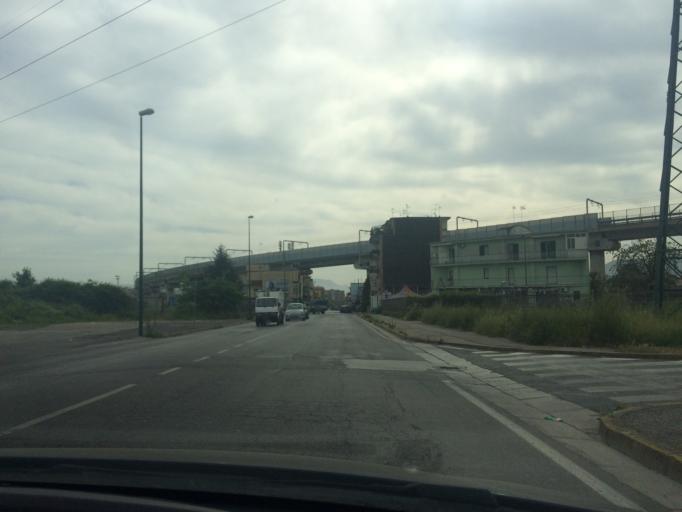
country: IT
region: Campania
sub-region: Provincia di Napoli
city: Mugnano di Napoli
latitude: 40.8939
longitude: 14.2244
